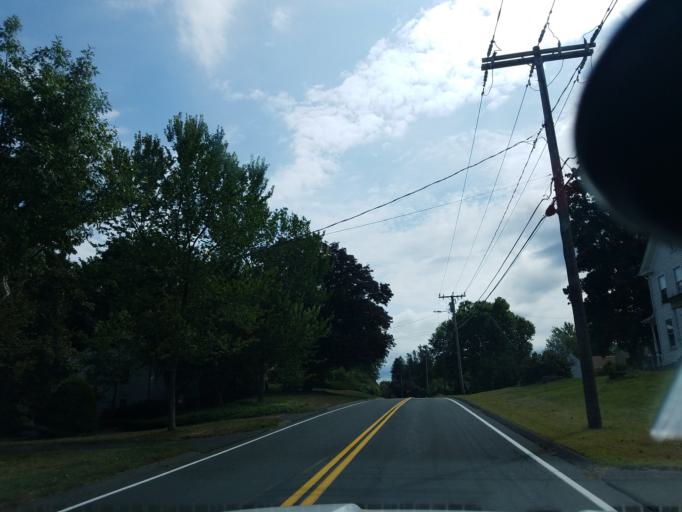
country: US
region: Connecticut
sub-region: Hartford County
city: Wethersfield
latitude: 41.6797
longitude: -72.6469
